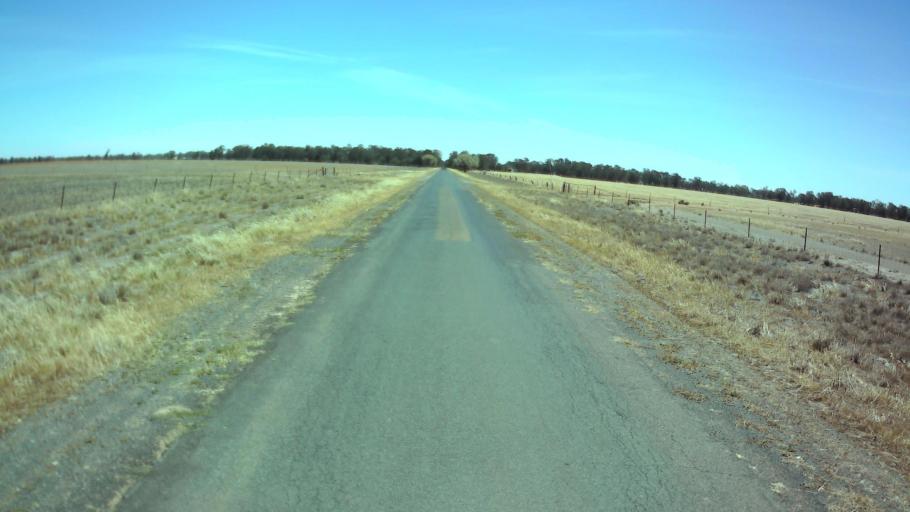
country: AU
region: New South Wales
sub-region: Weddin
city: Grenfell
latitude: -33.8606
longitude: 147.6938
